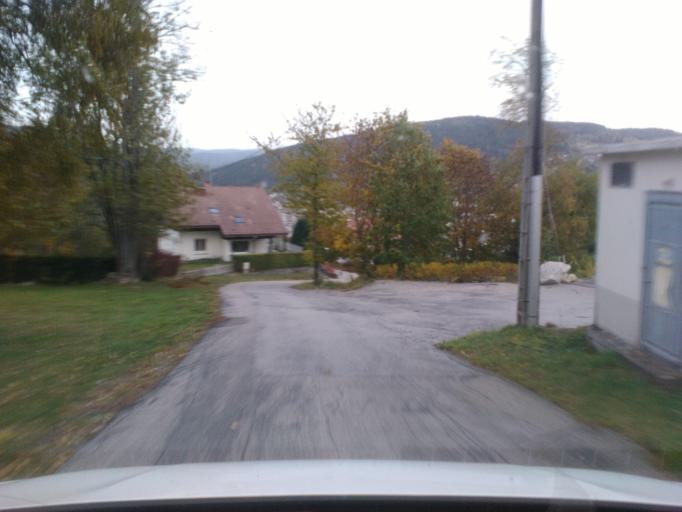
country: FR
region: Lorraine
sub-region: Departement des Vosges
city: Gerardmer
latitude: 48.0770
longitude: 6.8668
